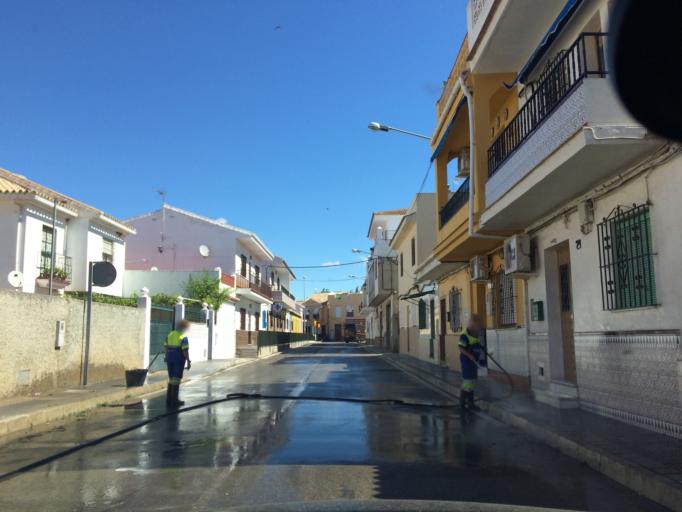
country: ES
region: Andalusia
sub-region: Provincia de Malaga
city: Alhaurin de la Torre
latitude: 36.7217
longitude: -4.5373
